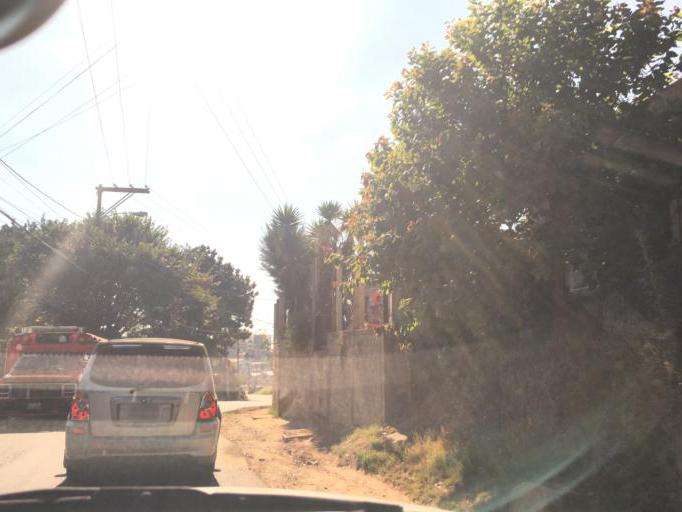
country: GT
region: Guatemala
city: Mixco
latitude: 14.6214
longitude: -90.6021
